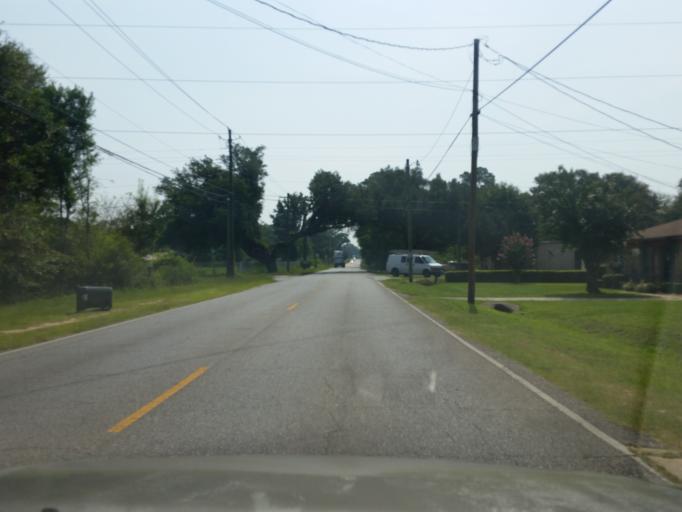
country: US
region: Florida
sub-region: Escambia County
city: Ensley
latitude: 30.5190
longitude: -87.2806
